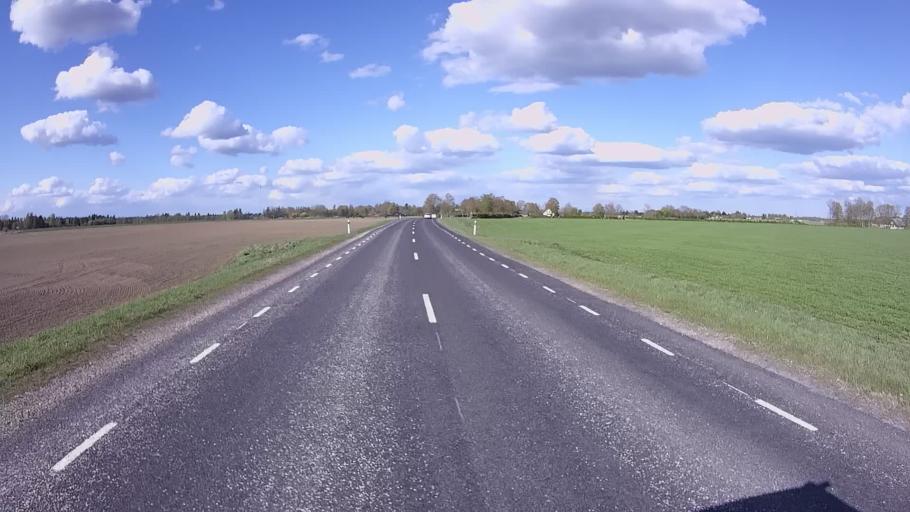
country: EE
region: Jogevamaa
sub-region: Jogeva linn
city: Jogeva
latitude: 58.7240
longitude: 26.1909
